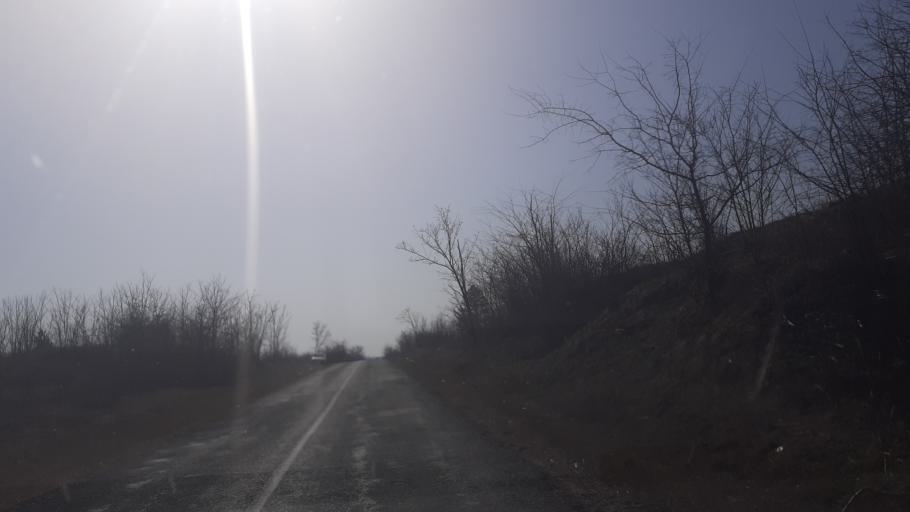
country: HU
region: Pest
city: Dabas
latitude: 47.1473
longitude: 19.3290
